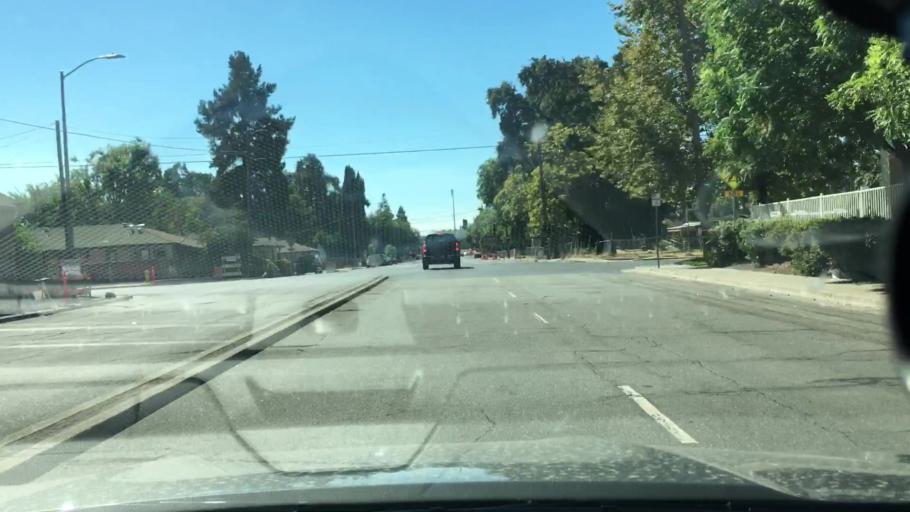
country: US
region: California
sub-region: Yolo County
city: West Sacramento
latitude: 38.5866
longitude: -121.5132
